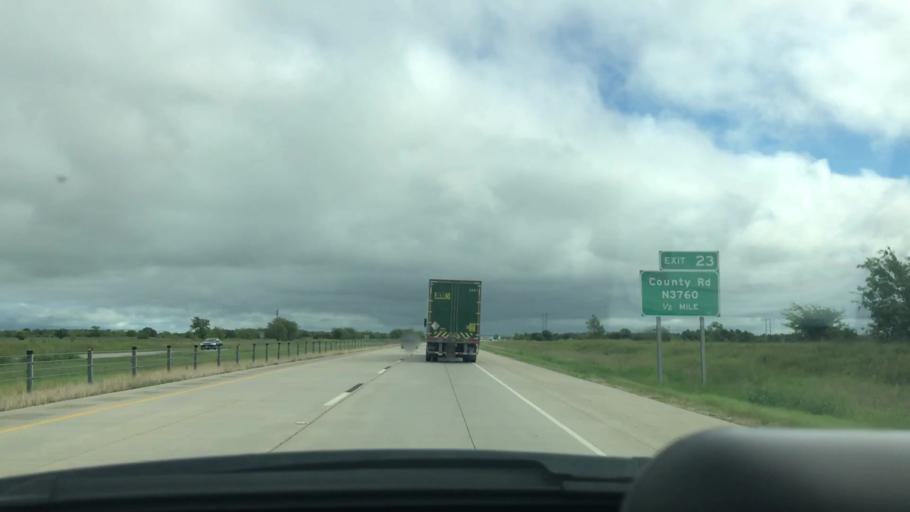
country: US
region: Oklahoma
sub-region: Bryan County
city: Durant
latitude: 34.0860
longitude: -96.3326
